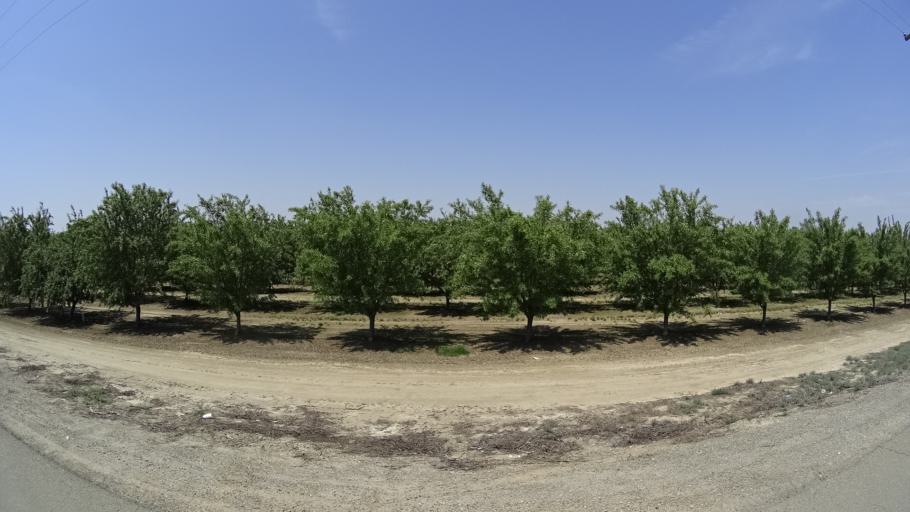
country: US
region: California
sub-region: Kings County
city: Lemoore
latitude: 36.3241
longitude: -119.7808
